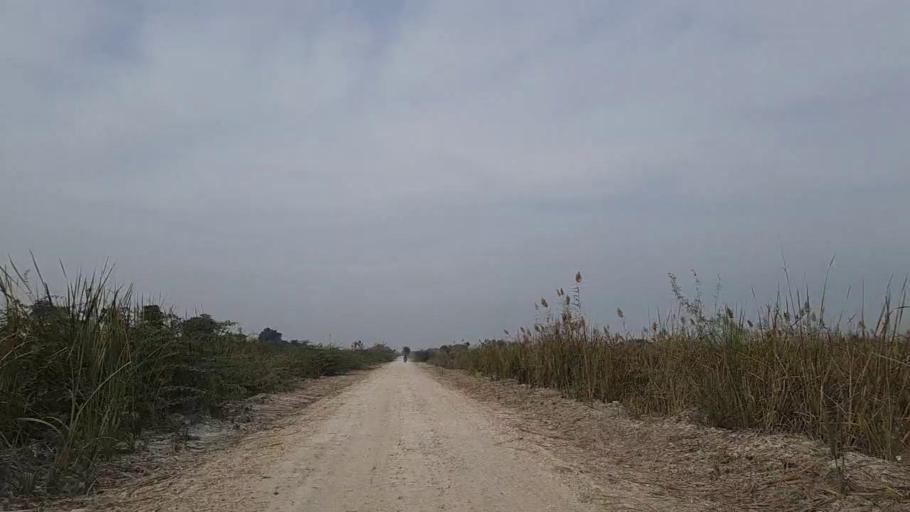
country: PK
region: Sindh
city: Daur
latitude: 26.4131
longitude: 68.4288
